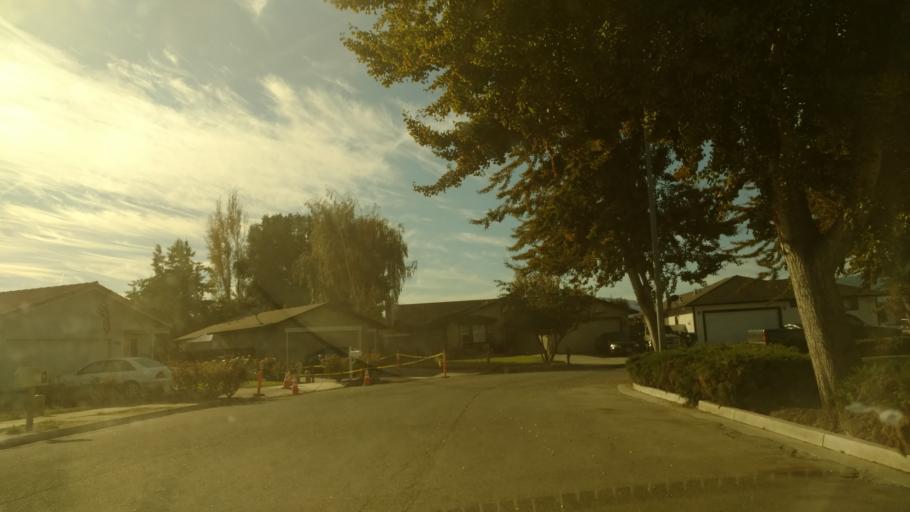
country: US
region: California
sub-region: San Benito County
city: Hollister
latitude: 36.8563
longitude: -121.4137
